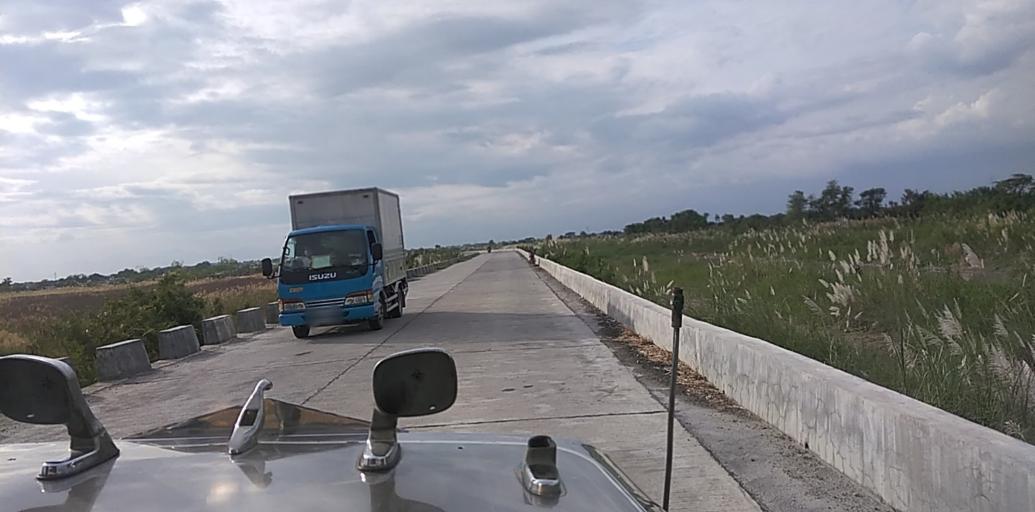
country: PH
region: Central Luzon
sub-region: Province of Pampanga
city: Minalin
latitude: 14.9671
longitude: 120.6671
